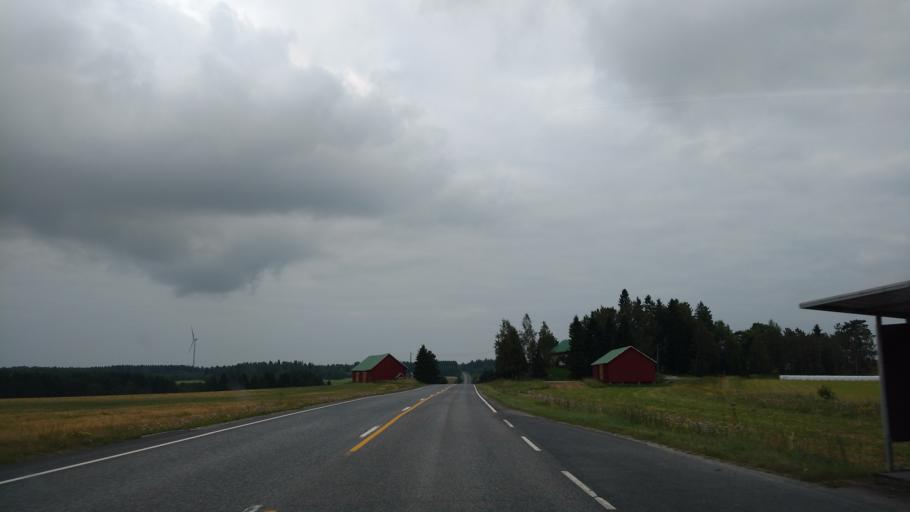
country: FI
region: Varsinais-Suomi
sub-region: Salo
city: Halikko
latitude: 60.4761
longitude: 23.0123
